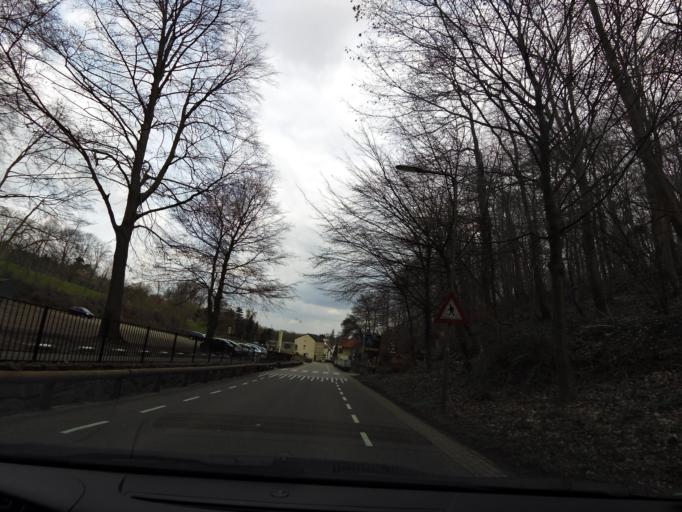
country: NL
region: Limburg
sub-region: Valkenburg aan de Geul
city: Sibbe
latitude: 50.8555
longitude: 5.8251
